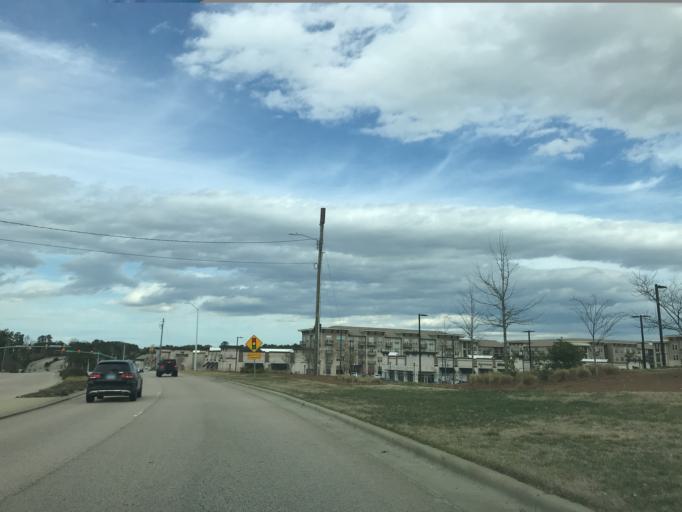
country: US
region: North Carolina
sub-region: Wake County
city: Morrisville
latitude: 35.7924
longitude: -78.8470
